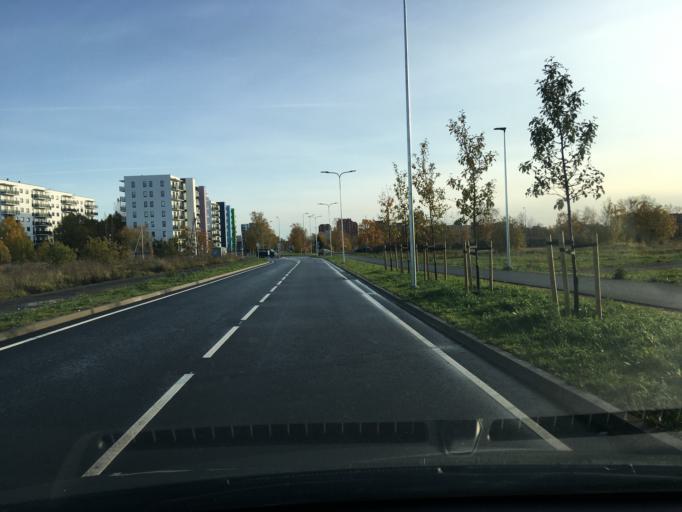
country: EE
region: Harju
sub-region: Viimsi vald
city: Viimsi
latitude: 59.4487
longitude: 24.8227
